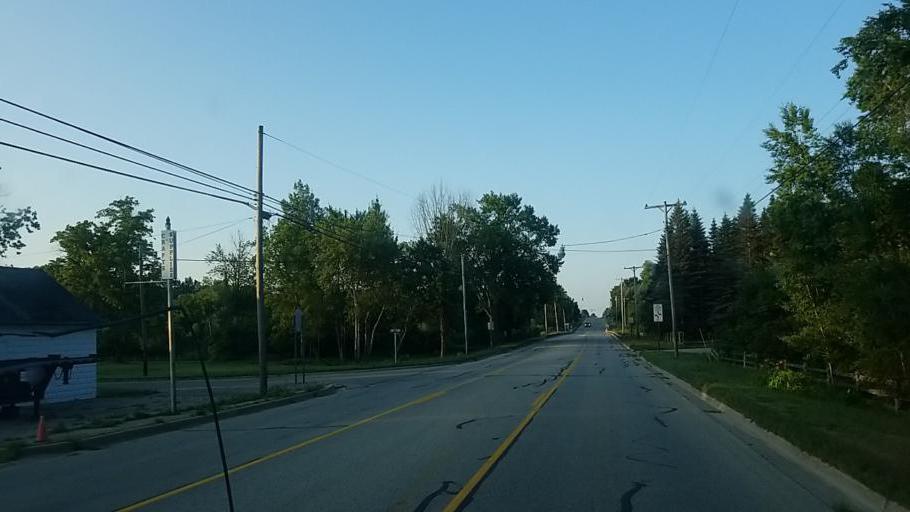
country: US
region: Michigan
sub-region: Isabella County
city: Lake Isabella
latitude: 43.7485
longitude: -85.1475
